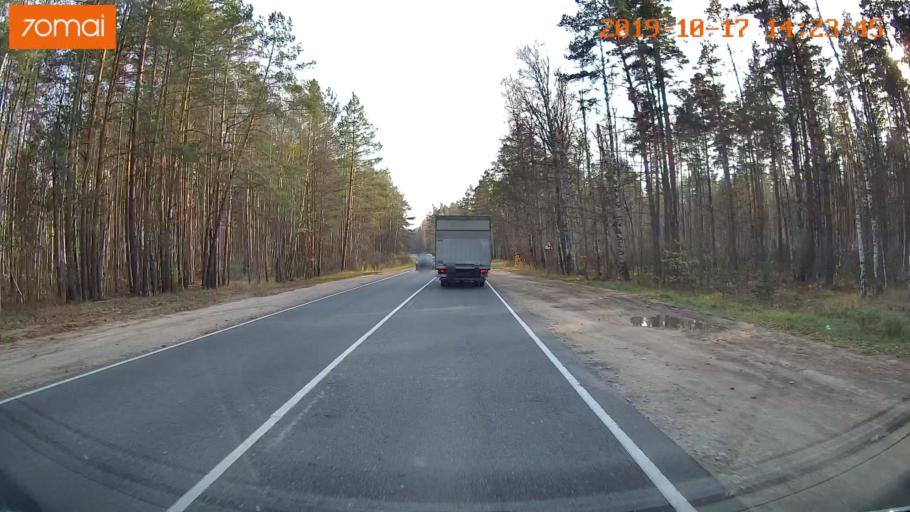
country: RU
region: Moskovskaya
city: Radovitskiy
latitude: 55.0156
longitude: 39.9621
